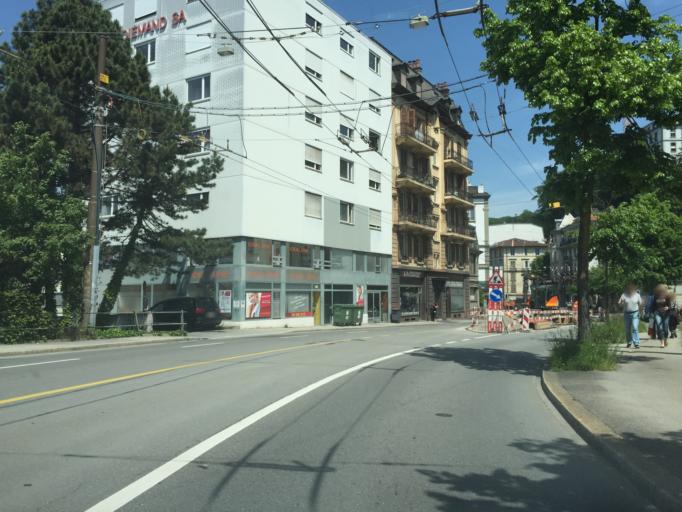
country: CH
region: Vaud
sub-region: Lausanne District
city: Lausanne
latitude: 46.5225
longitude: 6.6382
